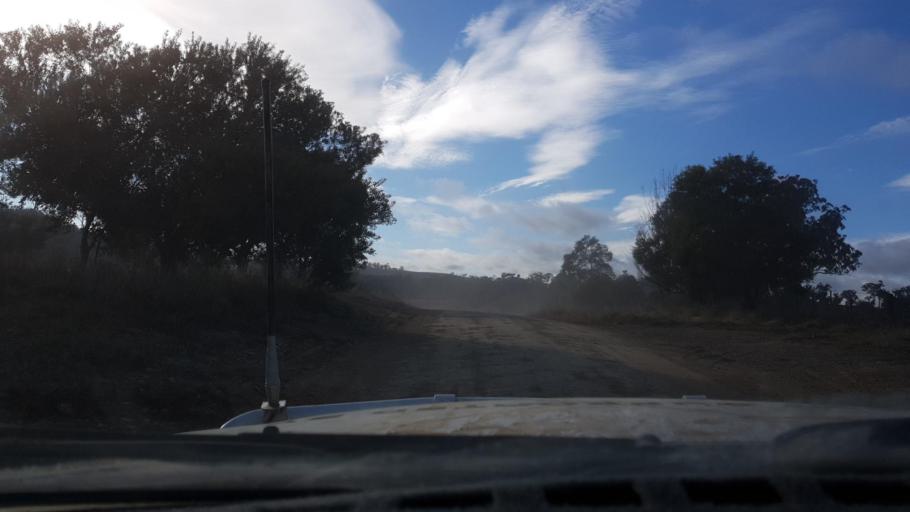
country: AU
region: New South Wales
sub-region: Armidale Dumaresq
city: Enmore
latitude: -30.7741
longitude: 151.6471
